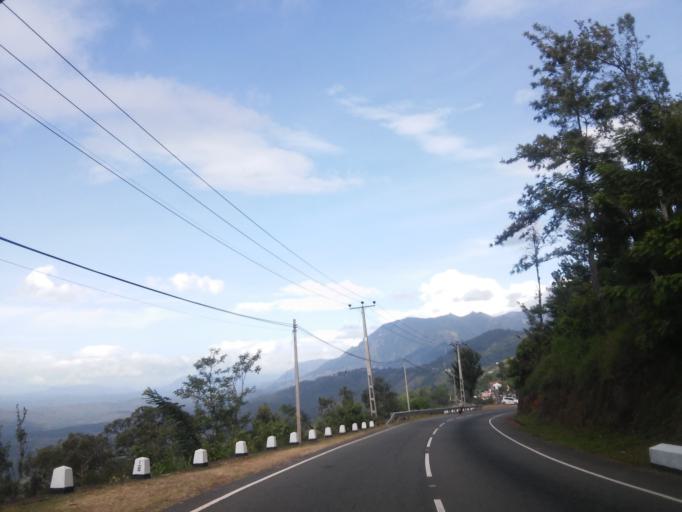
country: LK
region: Uva
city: Haputale
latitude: 6.7633
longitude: 80.9196
